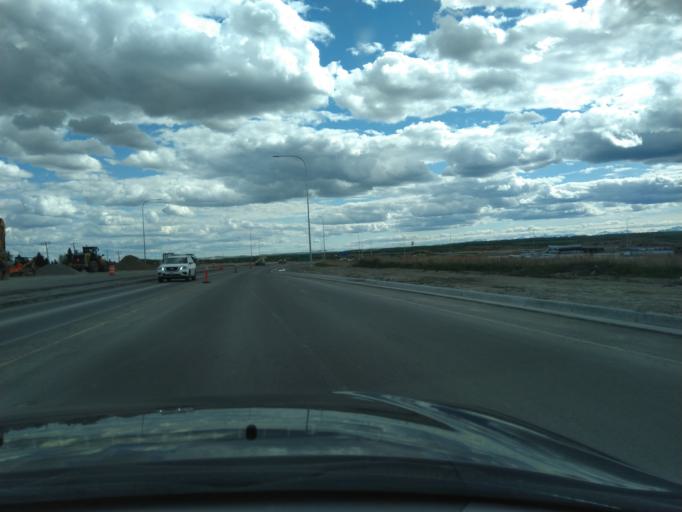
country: CA
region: Alberta
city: Calgary
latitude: 51.0064
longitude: -114.1419
